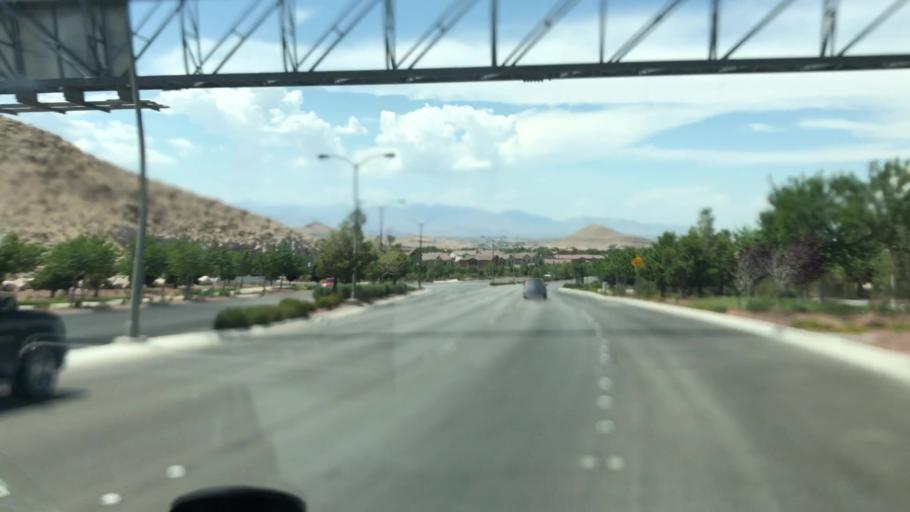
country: US
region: Nevada
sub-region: Clark County
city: Enterprise
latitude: 35.9621
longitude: -115.1849
